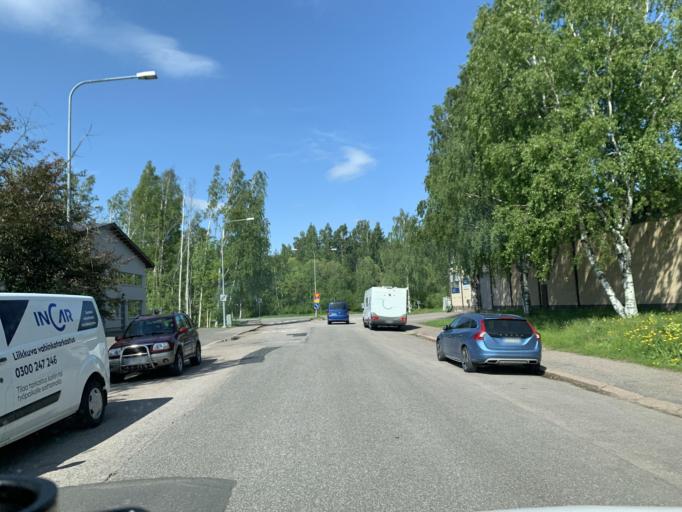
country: FI
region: Uusimaa
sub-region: Helsinki
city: Vantaa
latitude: 60.2557
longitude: 25.0271
